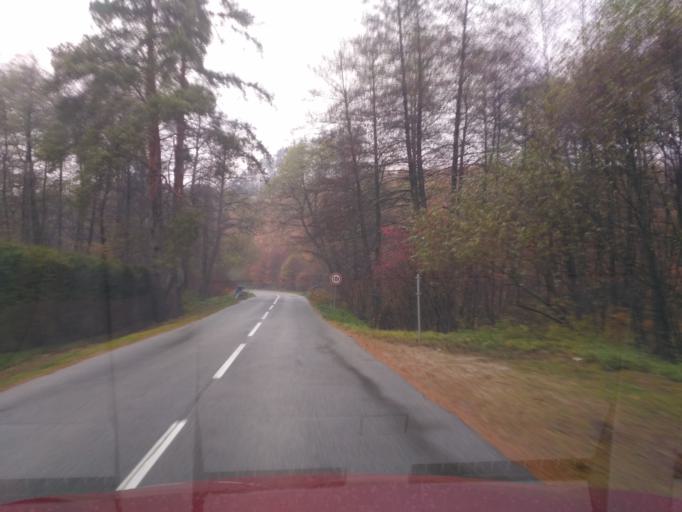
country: SK
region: Kosicky
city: Medzev
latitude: 48.7043
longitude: 20.8225
